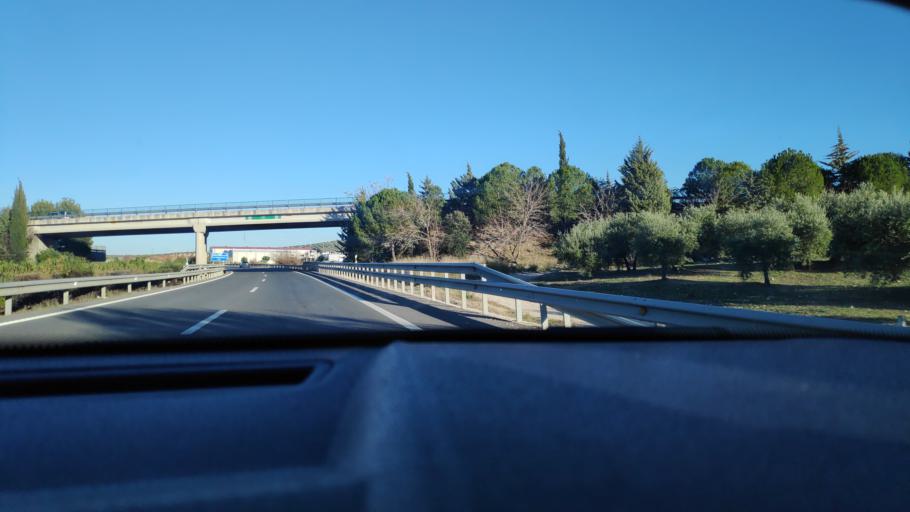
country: ES
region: Andalusia
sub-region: Provincia de Jaen
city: Torre del Campo
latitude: 37.7802
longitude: -3.8969
